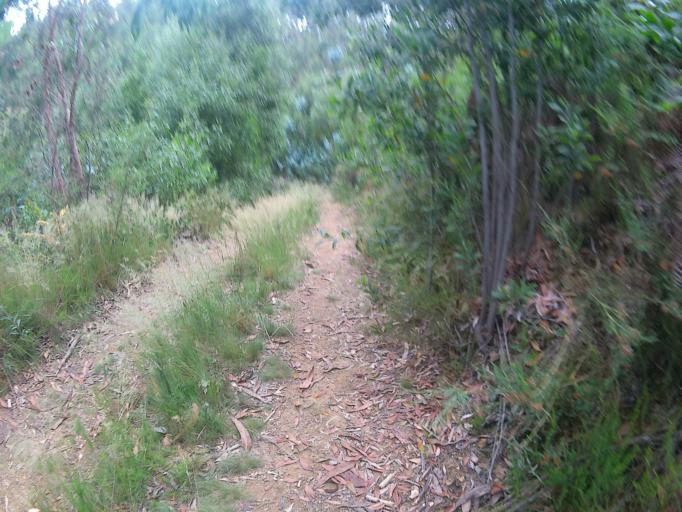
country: PT
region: Aveiro
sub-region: Albergaria-A-Velha
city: Branca
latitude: 40.7687
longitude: -8.4306
